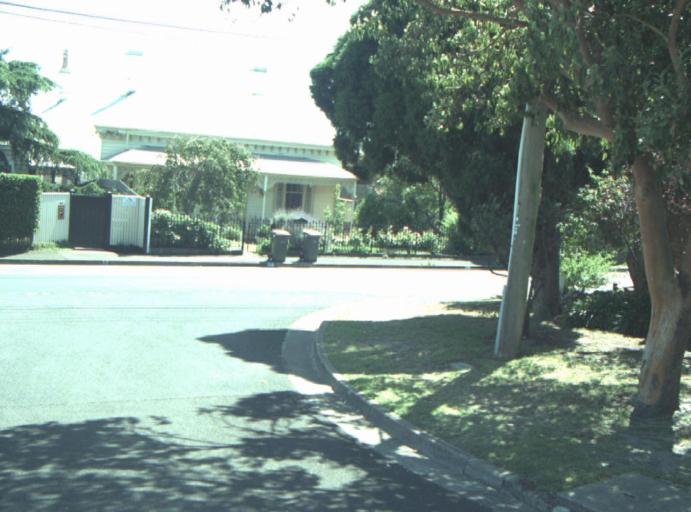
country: AU
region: Victoria
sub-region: Greater Geelong
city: Geelong West
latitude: -38.1479
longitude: 144.3453
